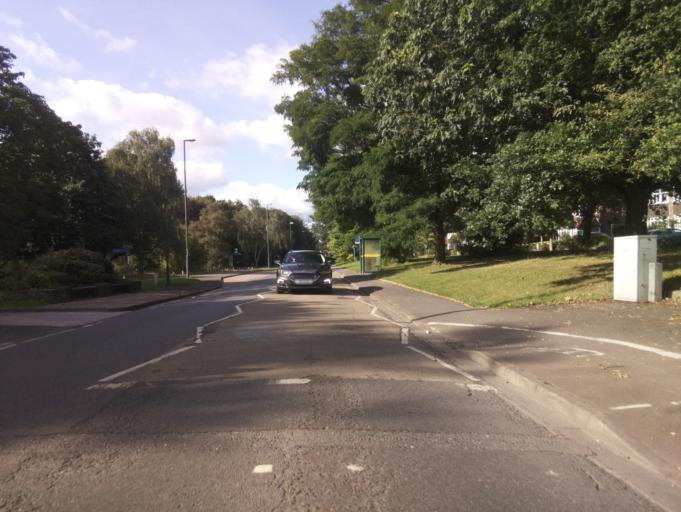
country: GB
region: England
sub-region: Derby
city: Derby
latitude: 52.9380
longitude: -1.5021
